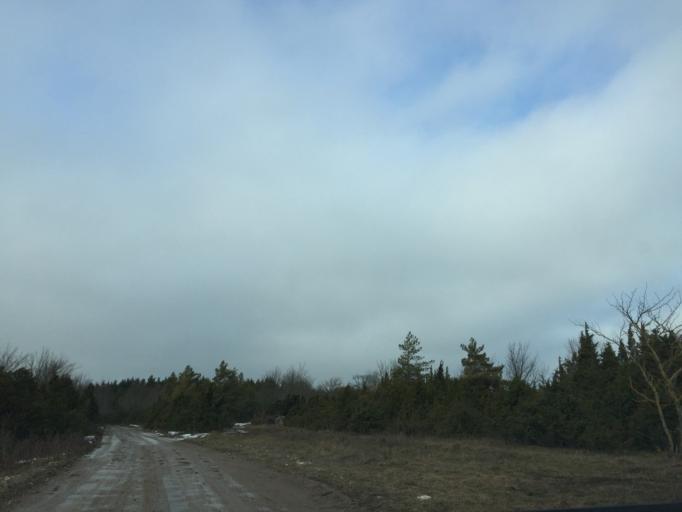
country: EE
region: Saare
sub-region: Kuressaare linn
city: Kuressaare
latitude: 58.4946
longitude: 21.9317
